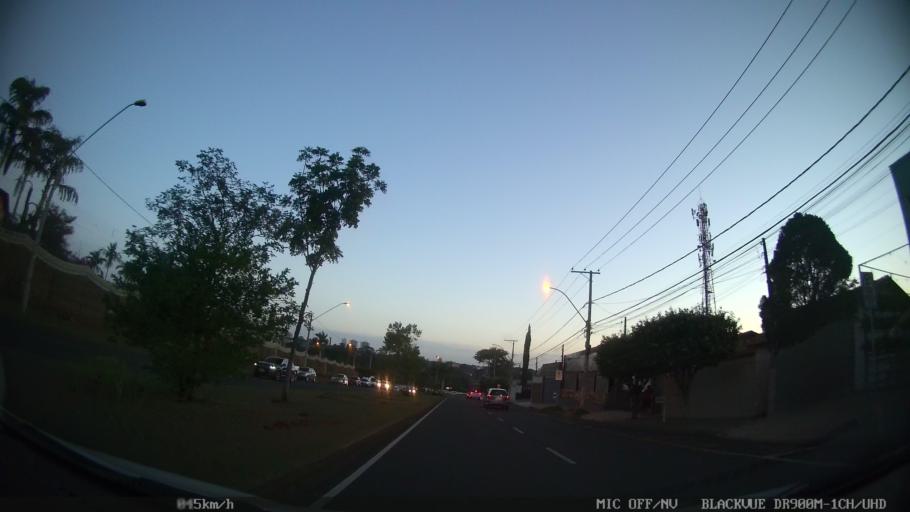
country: BR
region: Sao Paulo
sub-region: Sao Jose Do Rio Preto
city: Sao Jose do Rio Preto
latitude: -20.8096
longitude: -49.3511
